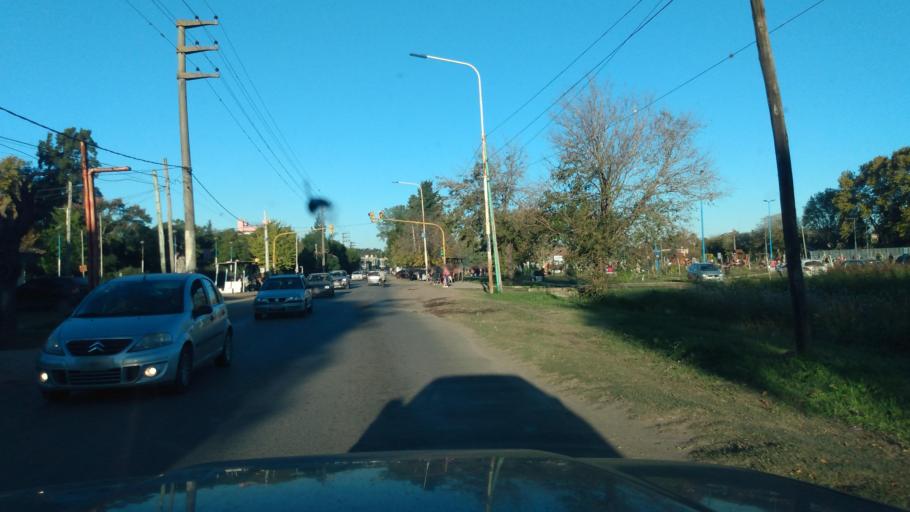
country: AR
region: Buenos Aires
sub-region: Partido de General Rodriguez
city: General Rodriguez
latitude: -34.6312
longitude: -58.8555
